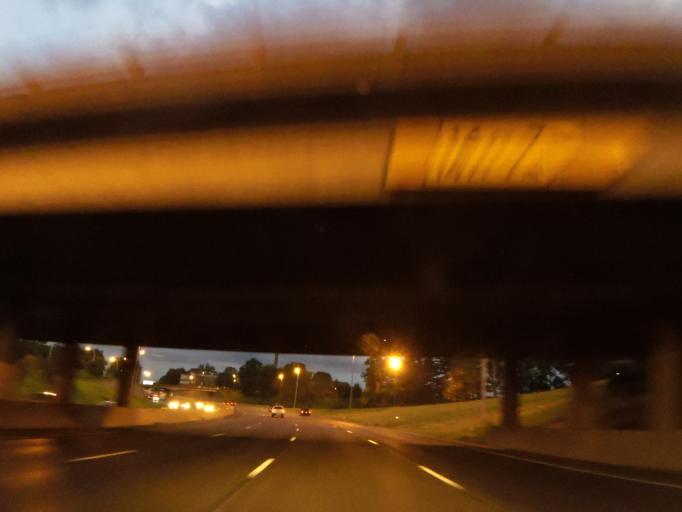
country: US
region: Missouri
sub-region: City of Saint Louis
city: St. Louis
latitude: 38.5970
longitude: -90.2162
